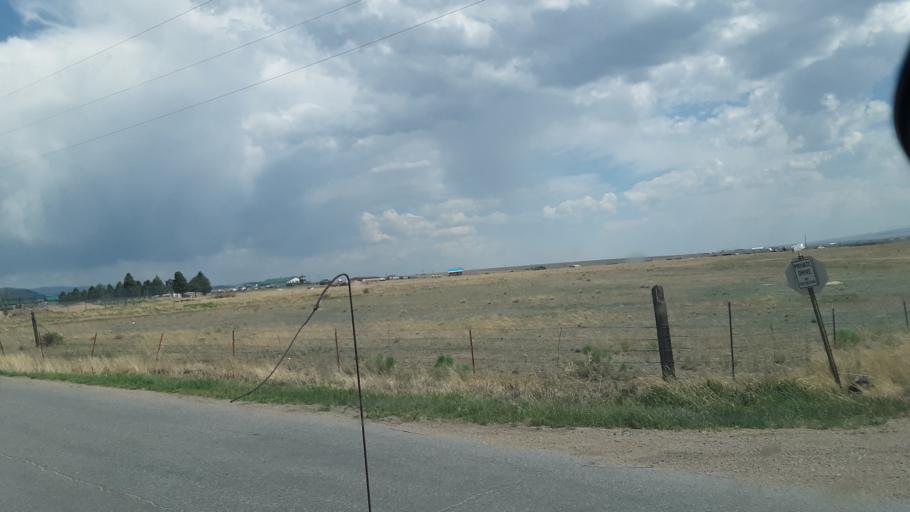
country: US
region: Colorado
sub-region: Custer County
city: Westcliffe
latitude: 38.1310
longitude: -105.4688
